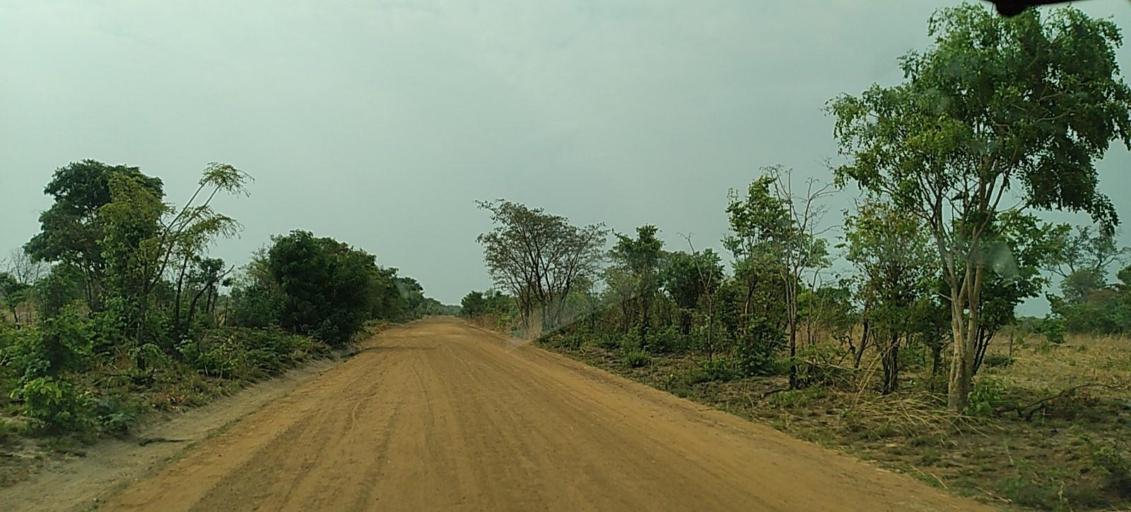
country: ZM
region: North-Western
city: Kabompo
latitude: -13.4397
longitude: 24.4234
